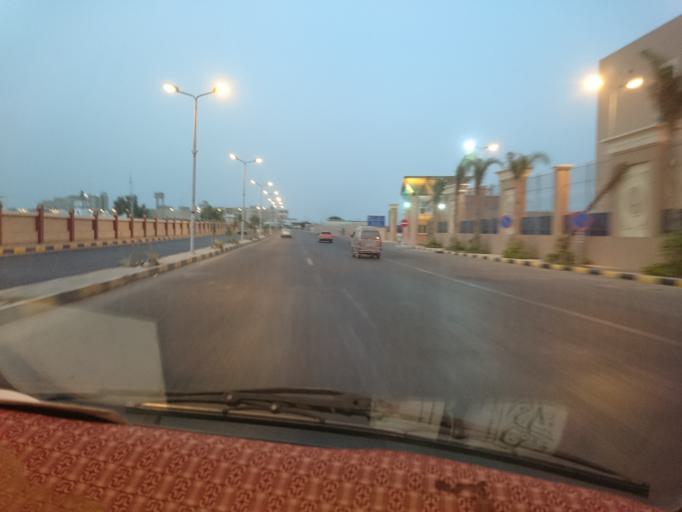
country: EG
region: Red Sea
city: Hurghada
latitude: 27.2321
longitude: 33.8458
